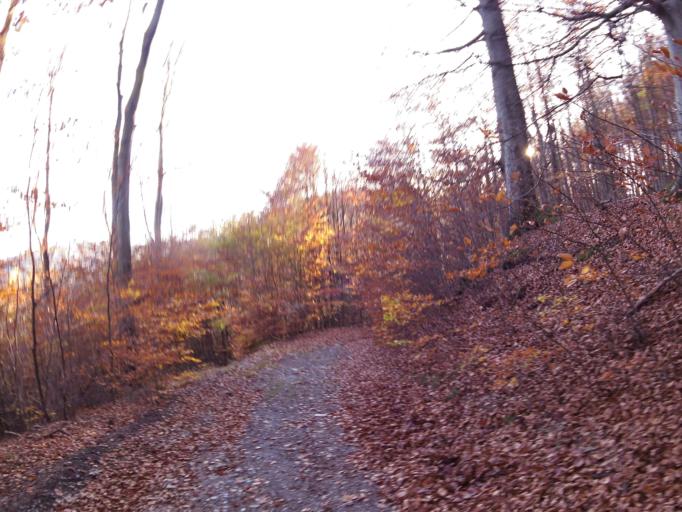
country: DE
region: Thuringia
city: Ruhla
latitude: 50.9016
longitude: 10.3624
